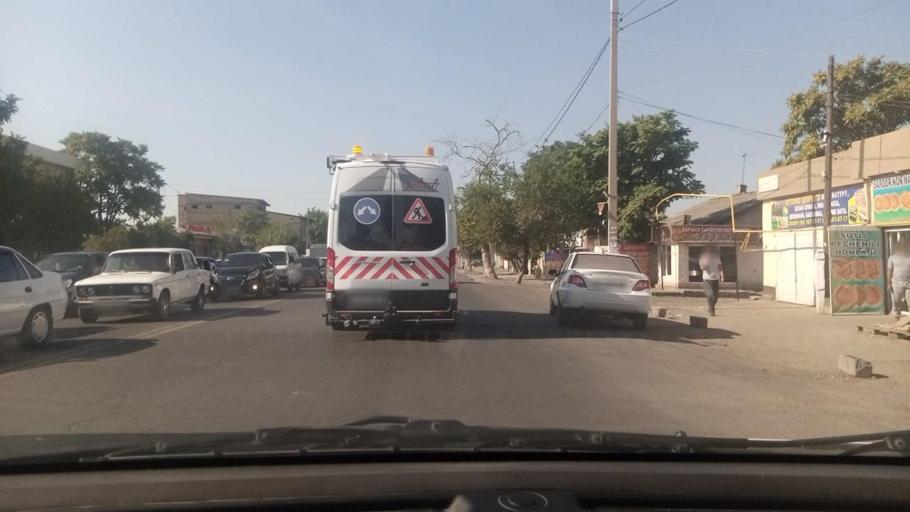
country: UZ
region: Toshkent Shahri
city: Bektemir
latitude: 41.2284
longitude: 69.3358
